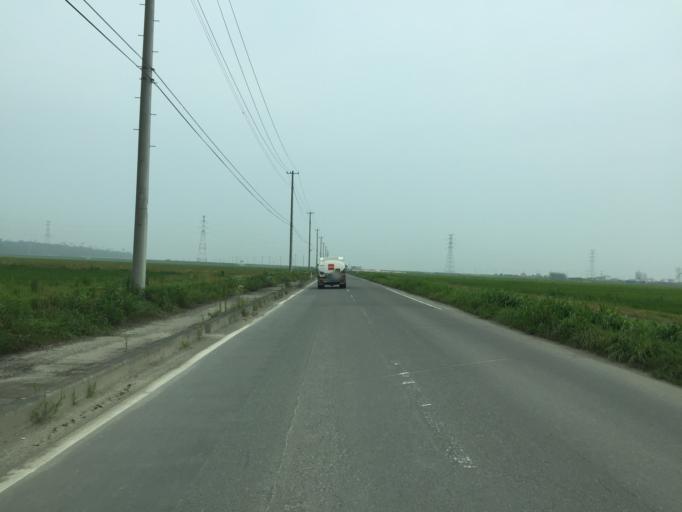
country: JP
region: Fukushima
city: Namie
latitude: 37.6384
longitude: 141.0051
